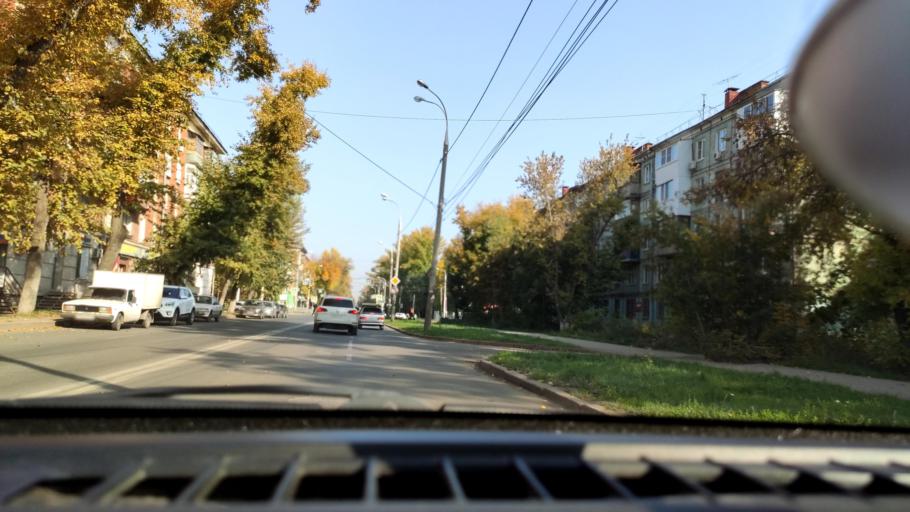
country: RU
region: Samara
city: Samara
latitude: 53.2106
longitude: 50.2484
